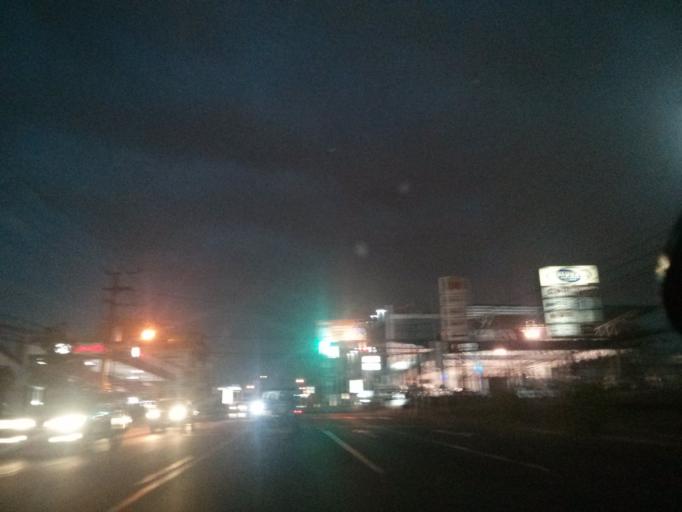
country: CR
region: San Jose
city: Colima
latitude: 9.9484
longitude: -84.0958
